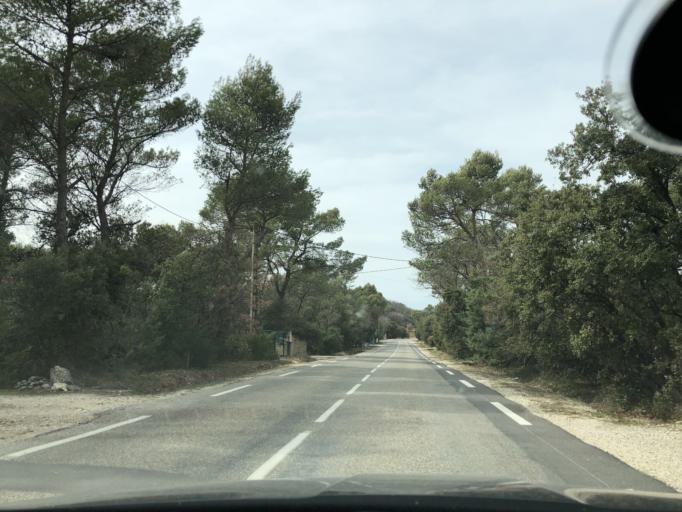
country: FR
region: Provence-Alpes-Cote d'Azur
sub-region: Departement du Vaucluse
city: Goult
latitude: 43.8277
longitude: 5.2442
